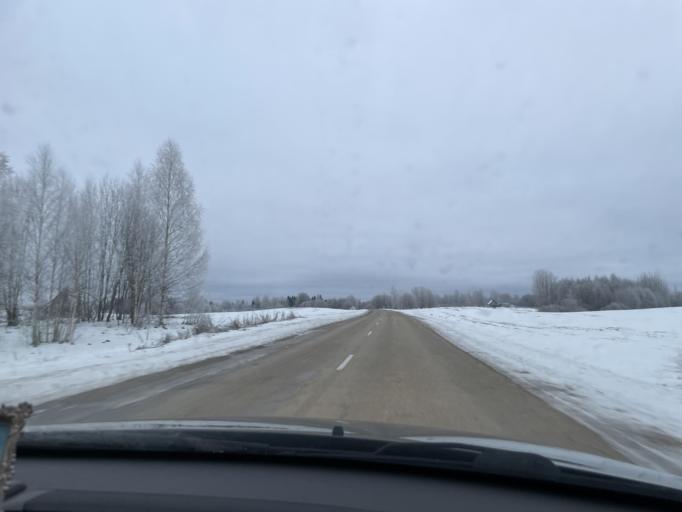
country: LV
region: Rezekne
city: Rezekne
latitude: 56.4398
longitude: 27.5083
